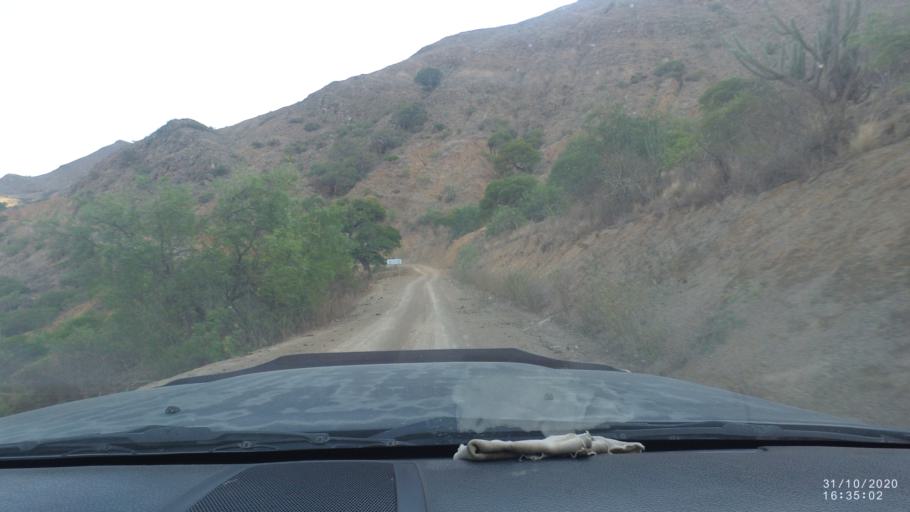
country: BO
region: Chuquisaca
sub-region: Provincia Zudanez
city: Mojocoya
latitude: -18.4511
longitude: -64.5833
